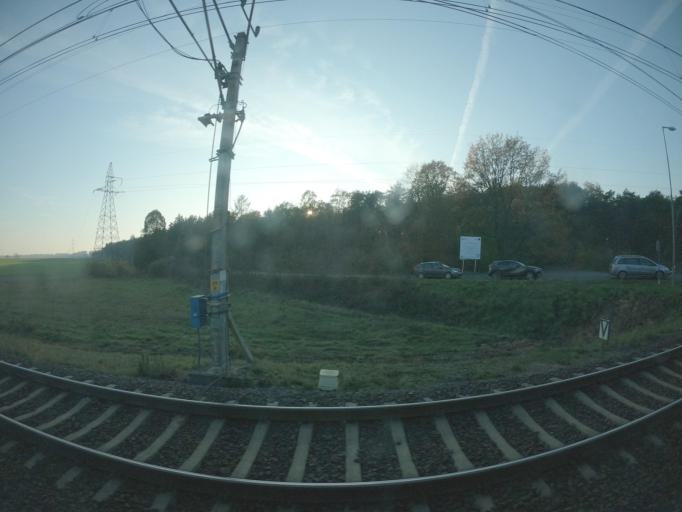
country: PL
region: Lubusz
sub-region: Powiat slubicki
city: Rzepin
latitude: 52.3012
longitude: 14.8740
